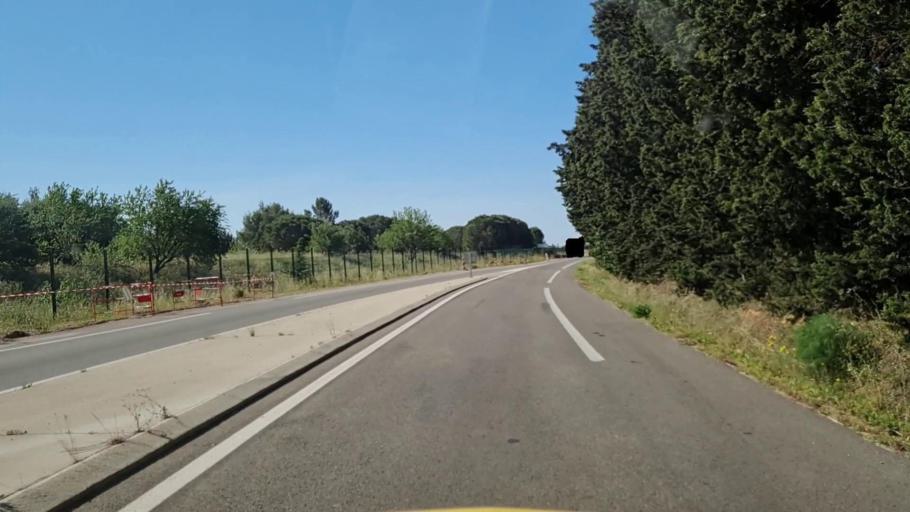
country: FR
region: Languedoc-Roussillon
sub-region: Departement du Gard
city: Garons
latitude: 43.7475
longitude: 4.4091
